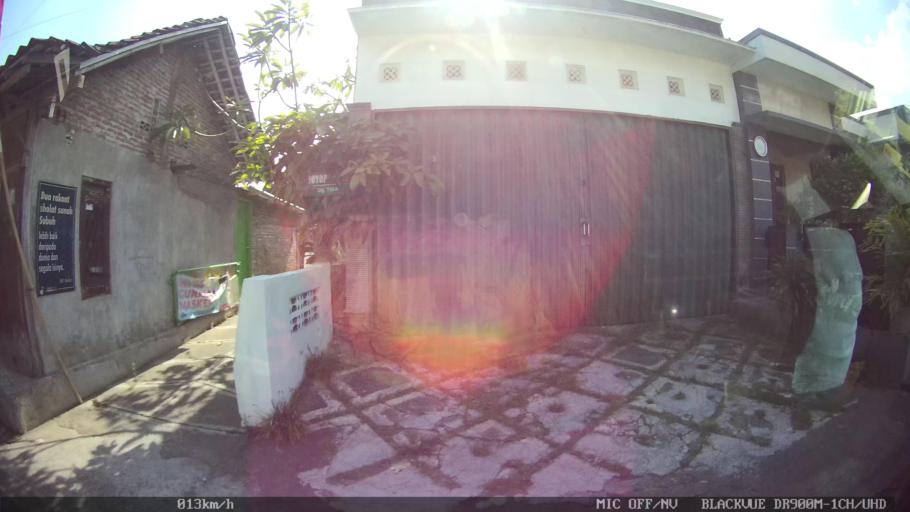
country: ID
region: Daerah Istimewa Yogyakarta
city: Sewon
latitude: -7.8322
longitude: 110.4019
